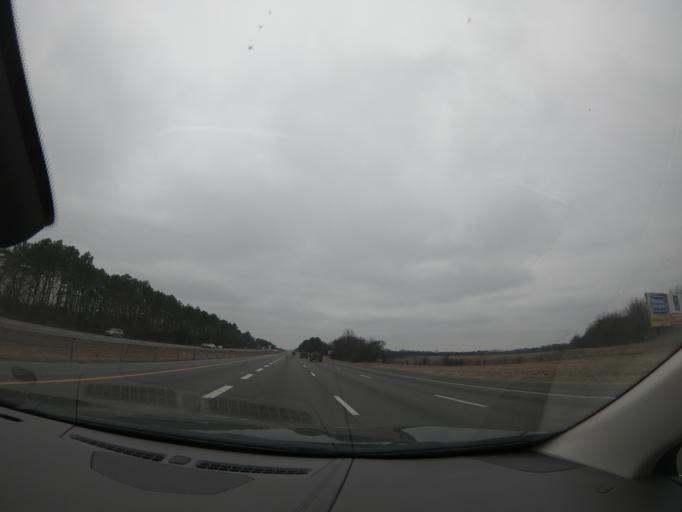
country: US
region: Tennessee
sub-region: Rutherford County
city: Smyrna
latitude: 35.9002
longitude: -86.4933
